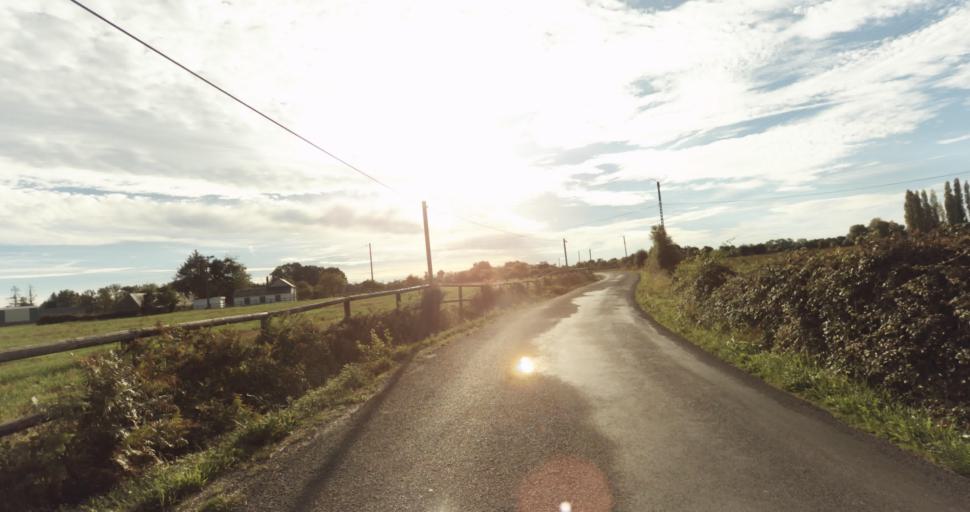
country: FR
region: Lower Normandy
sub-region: Departement de l'Orne
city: Vimoutiers
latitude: 48.8834
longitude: 0.2471
